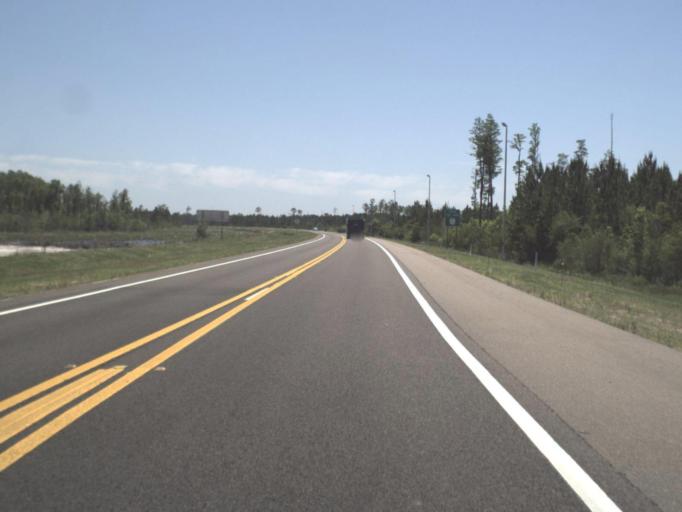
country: US
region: Florida
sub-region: Duval County
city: Baldwin
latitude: 30.2741
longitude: -81.8754
